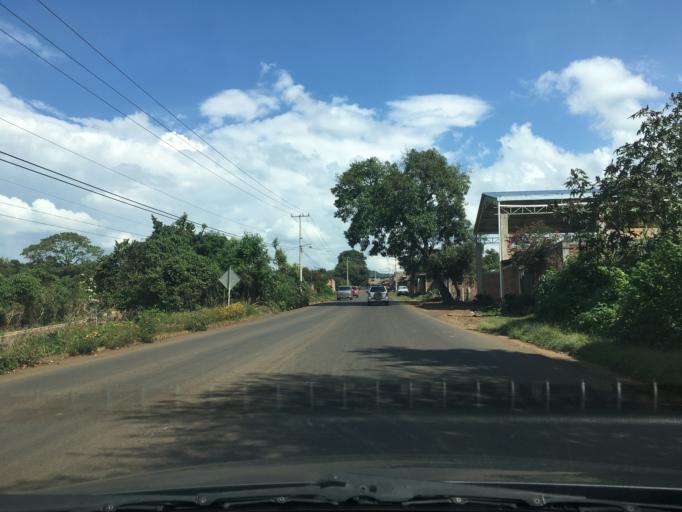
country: MX
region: Michoacan
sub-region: Tingueindin
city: Tingueindin
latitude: 19.8432
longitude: -102.4734
